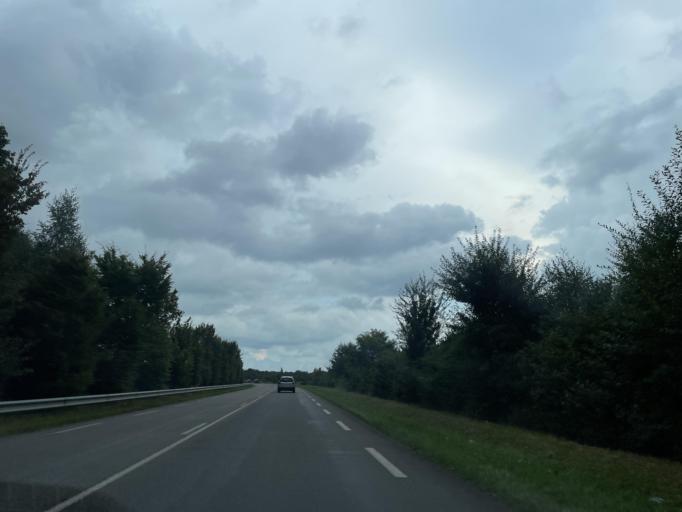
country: FR
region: Haute-Normandie
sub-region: Departement de la Seine-Maritime
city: Forges-les-Eaux
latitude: 49.5998
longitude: 1.5299
